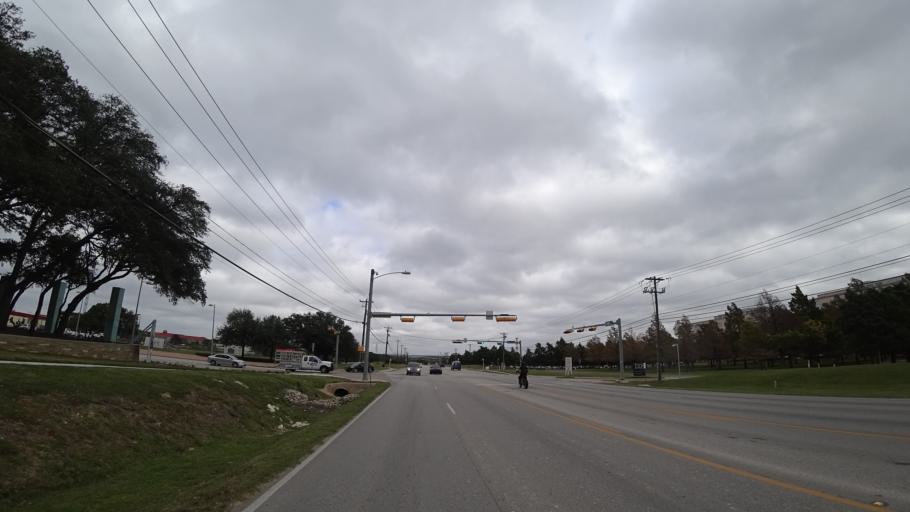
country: US
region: Texas
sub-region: Travis County
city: Wells Branch
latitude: 30.4019
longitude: -97.7180
